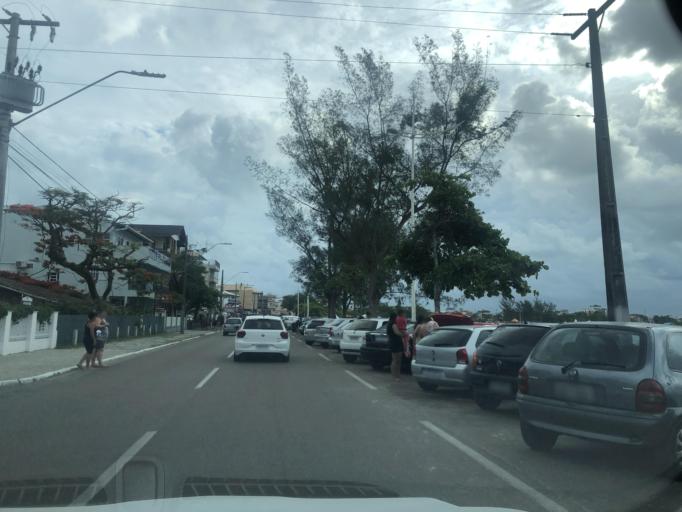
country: BR
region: Santa Catarina
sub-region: Sao Francisco Do Sul
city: Sao Francisco do Sul
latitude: -26.2244
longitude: -48.5018
